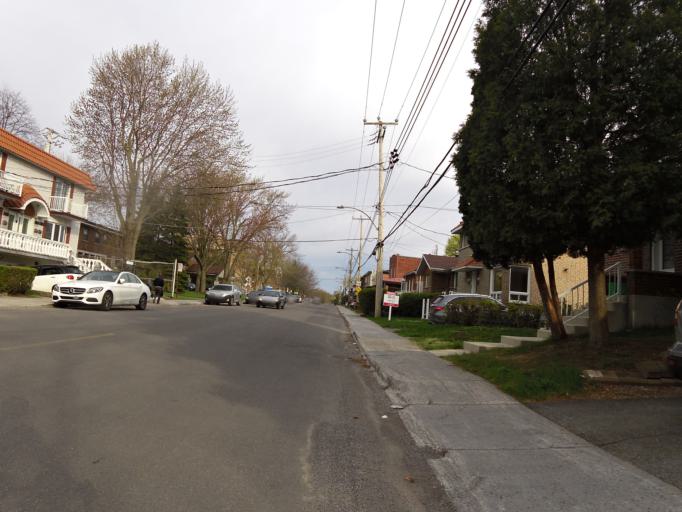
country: CA
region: Quebec
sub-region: Laval
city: Laval
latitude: 45.5407
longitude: -73.6873
